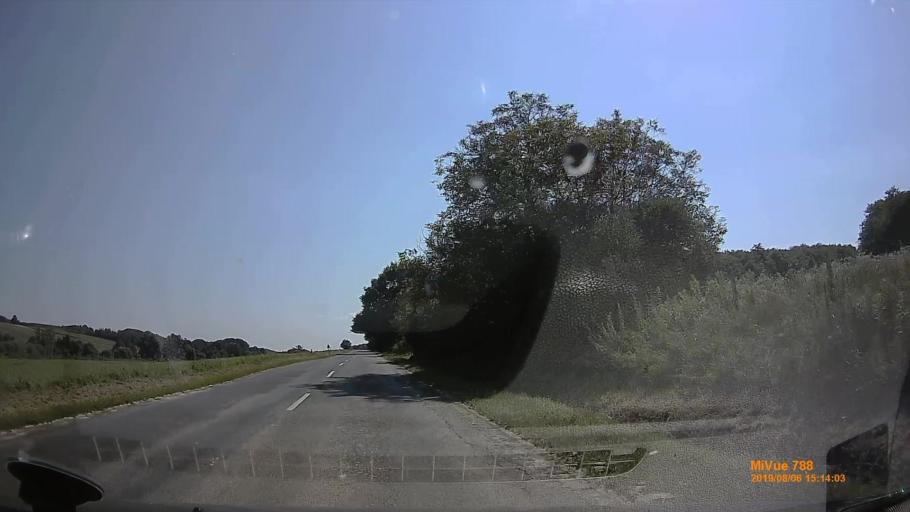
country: HU
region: Zala
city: Murakeresztur
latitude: 46.3456
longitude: 16.9757
